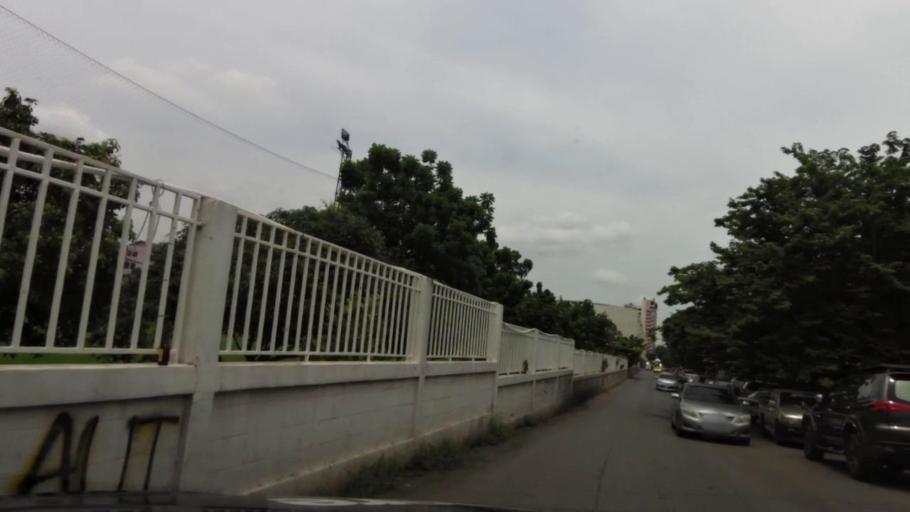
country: TH
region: Bangkok
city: Bang Kapi
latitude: 13.7711
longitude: 100.6432
